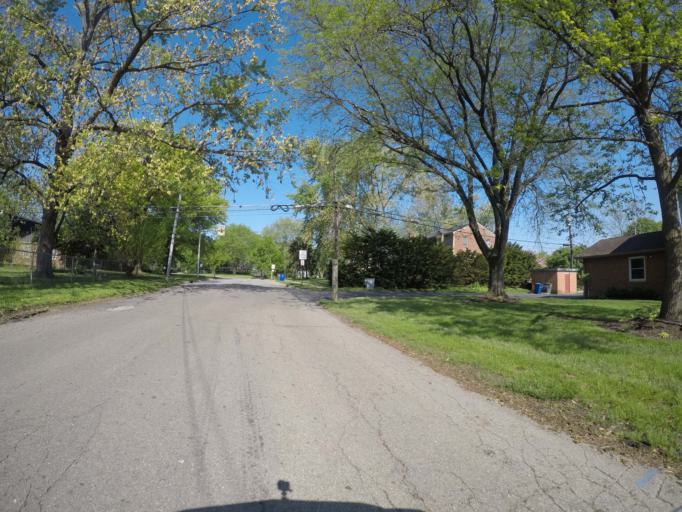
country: US
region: Ohio
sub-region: Franklin County
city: Upper Arlington
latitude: 40.0331
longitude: -83.0460
